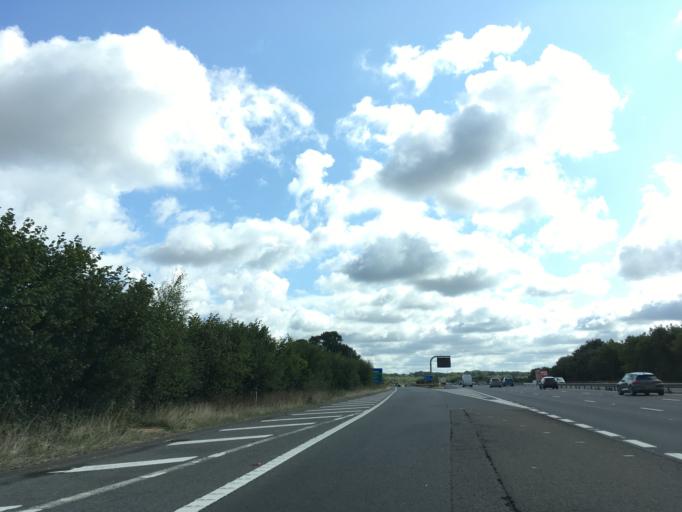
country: GB
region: England
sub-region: West Berkshire
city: Winterbourne
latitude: 51.4530
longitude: -1.3205
